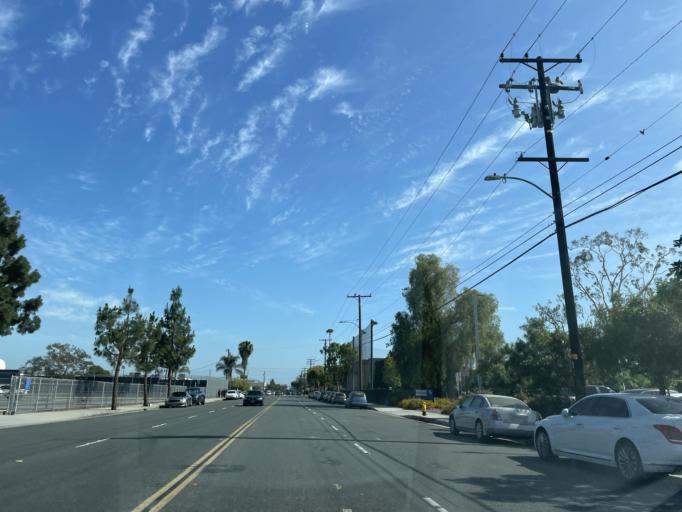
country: US
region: California
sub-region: Los Angeles County
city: Norwalk
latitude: 33.9072
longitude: -118.0554
